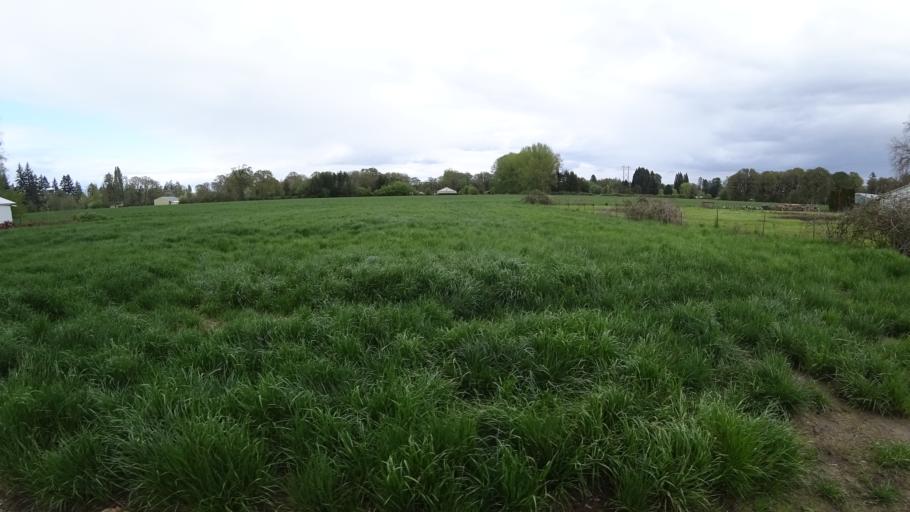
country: US
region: Oregon
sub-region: Washington County
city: Hillsboro
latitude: 45.5587
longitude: -122.9584
